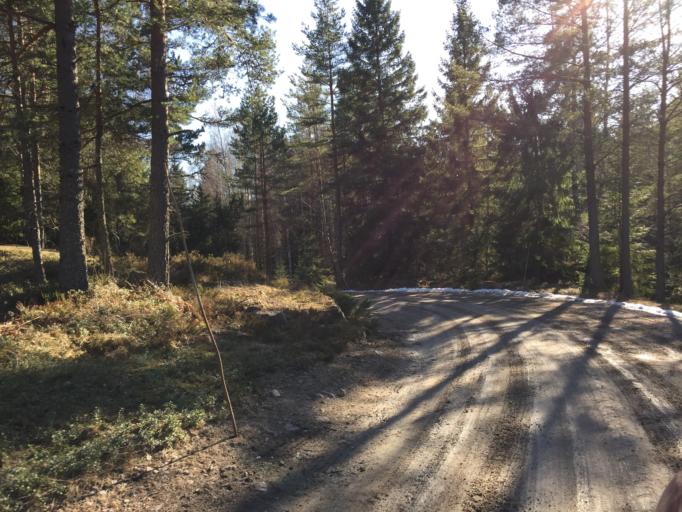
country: SE
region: OErebro
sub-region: Orebro Kommun
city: Odensbacken
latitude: 58.9810
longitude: 15.6347
